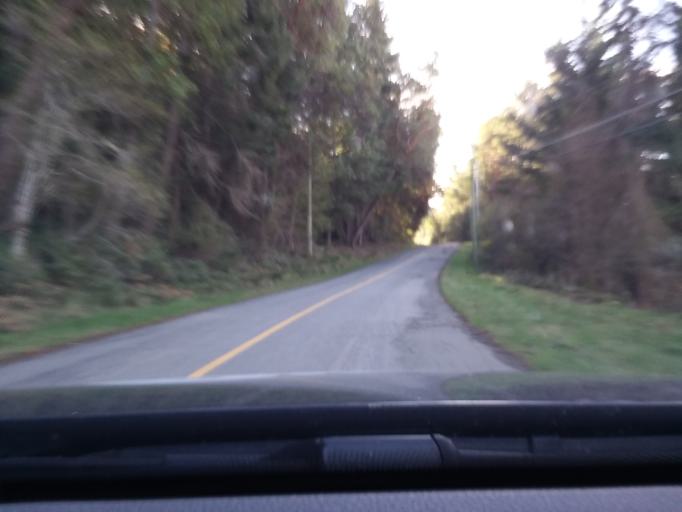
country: CA
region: British Columbia
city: North Cowichan
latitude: 48.9645
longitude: -123.5504
